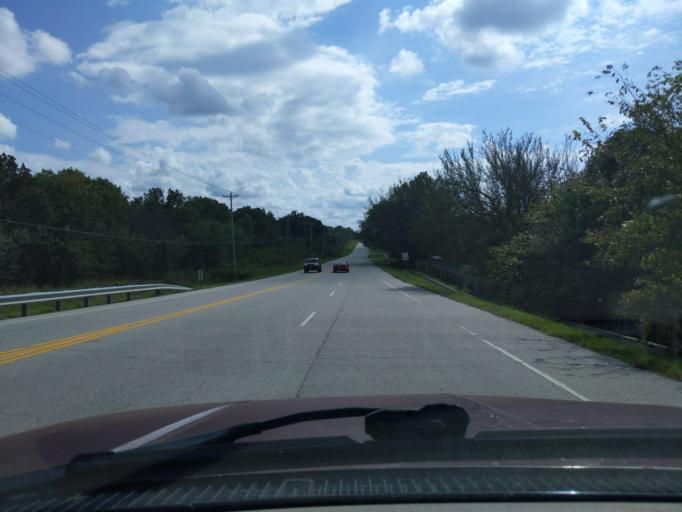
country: US
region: Oklahoma
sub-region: Tulsa County
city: Oakhurst
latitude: 36.0738
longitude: -96.0117
